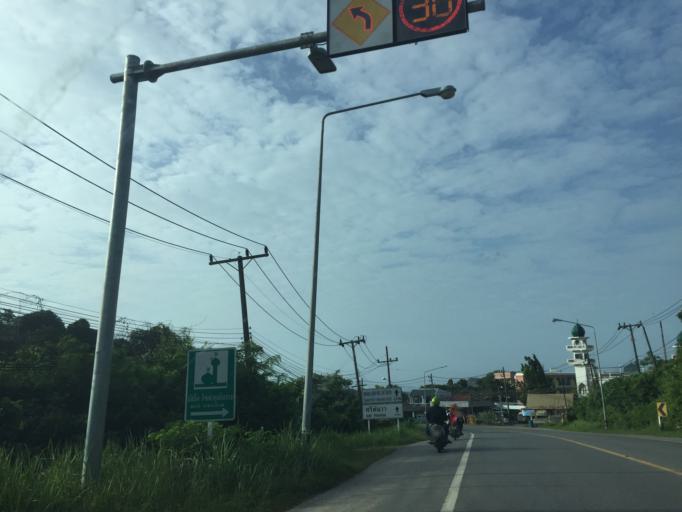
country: TH
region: Phuket
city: Mueang Phuket
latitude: 7.8302
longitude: 98.4011
